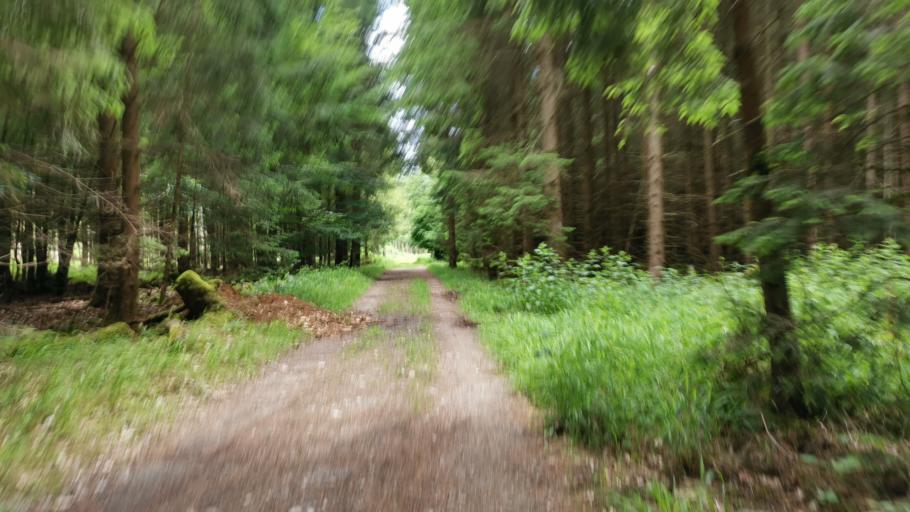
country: DE
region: Bavaria
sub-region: Upper Bavaria
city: Pullach im Isartal
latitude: 48.0582
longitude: 11.4975
